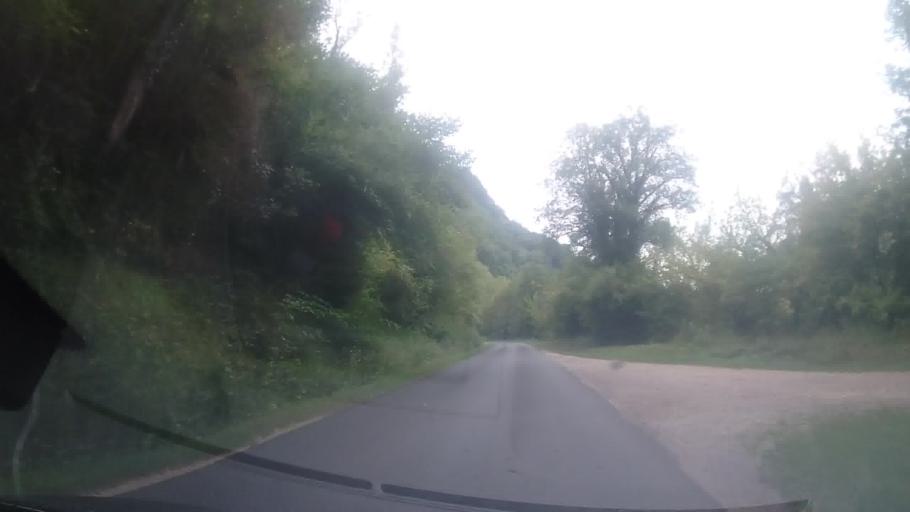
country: FR
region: Aquitaine
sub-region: Departement de la Dordogne
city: Domme
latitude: 44.8061
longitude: 1.2211
